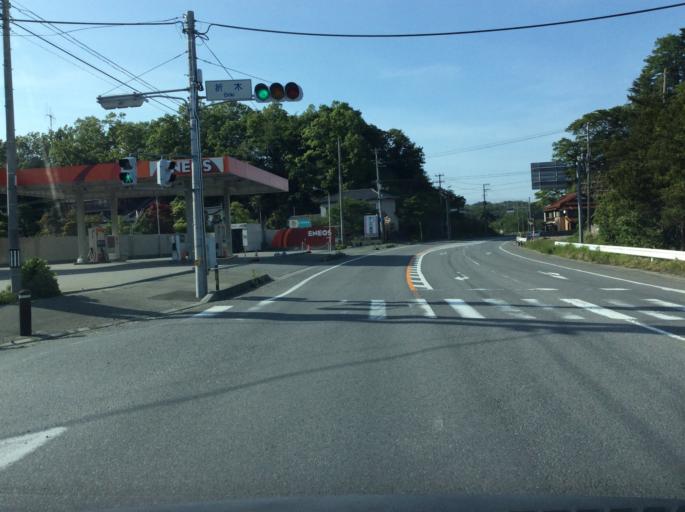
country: JP
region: Fukushima
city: Iwaki
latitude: 37.2033
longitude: 140.9926
